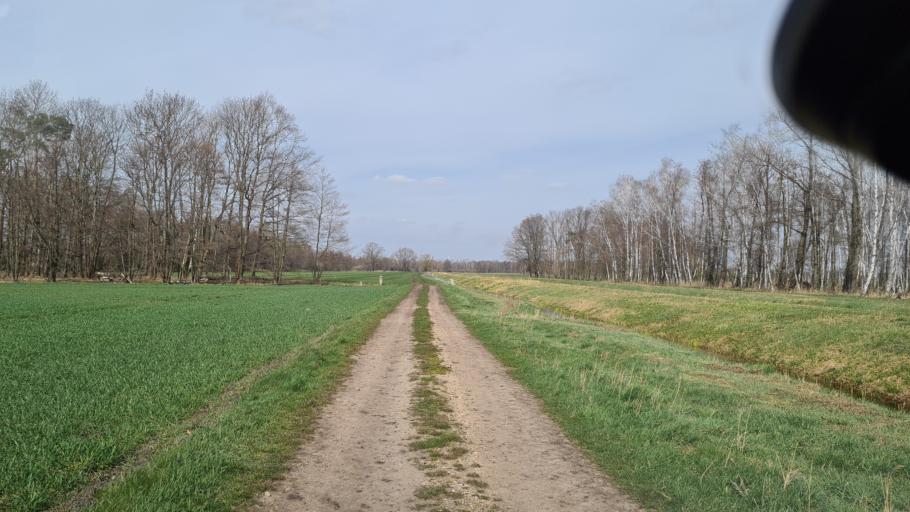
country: DE
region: Brandenburg
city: Bronkow
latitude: 51.6213
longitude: 13.9170
